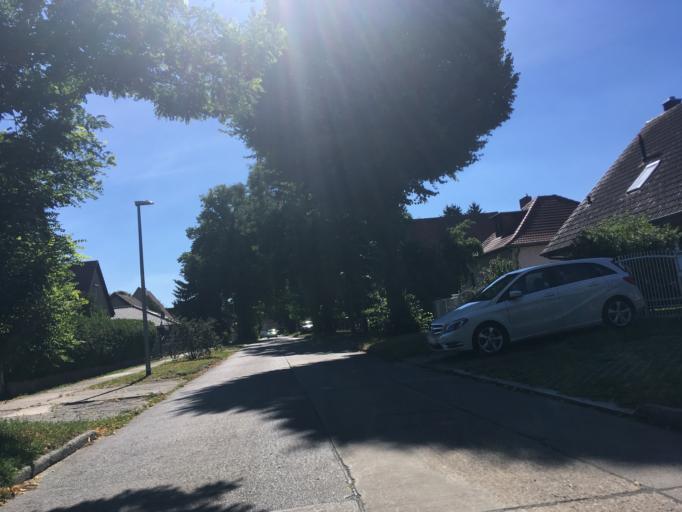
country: DE
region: Brandenburg
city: Petershagen
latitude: 52.5307
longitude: 13.7519
